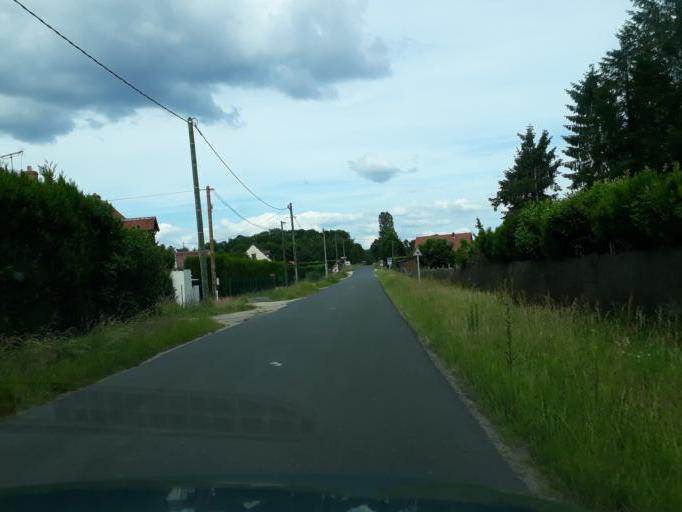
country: FR
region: Centre
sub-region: Departement du Loiret
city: Menestreau-en-Villette
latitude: 47.7192
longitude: 2.0171
